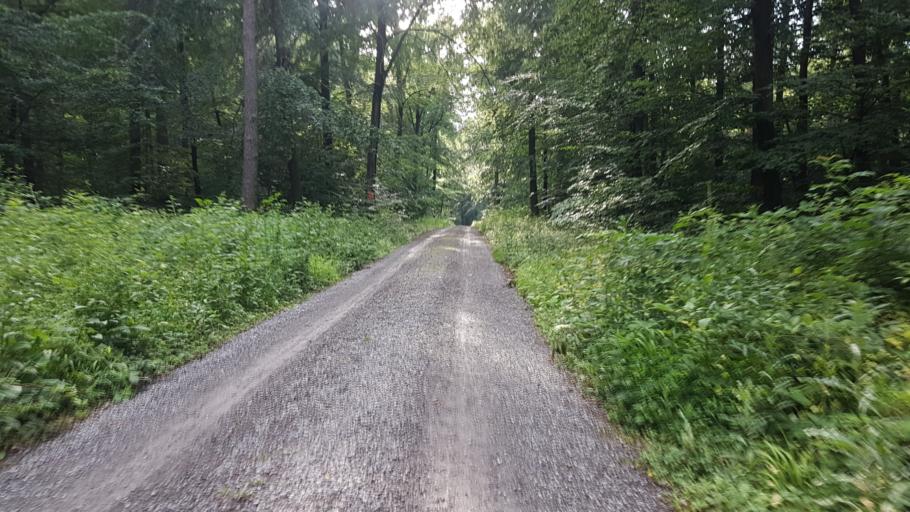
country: DE
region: Baden-Wuerttemberg
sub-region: Regierungsbezirk Stuttgart
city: Zaberfeld
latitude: 49.0382
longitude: 8.9144
